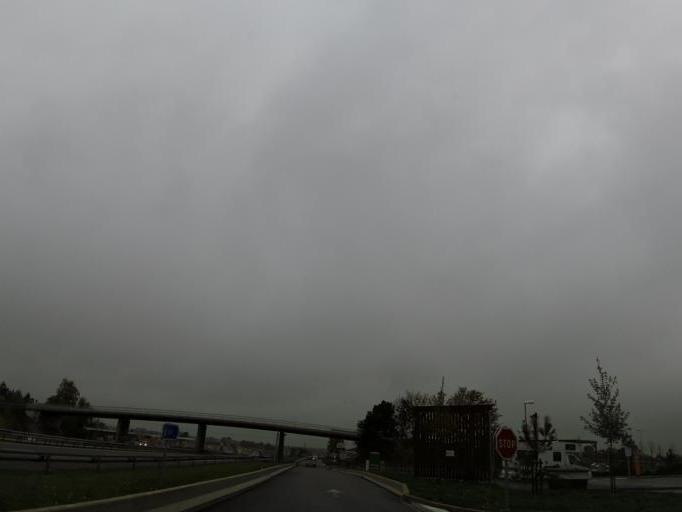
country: FR
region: Champagne-Ardenne
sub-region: Departement de la Marne
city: Verzy
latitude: 49.1188
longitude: 4.2461
